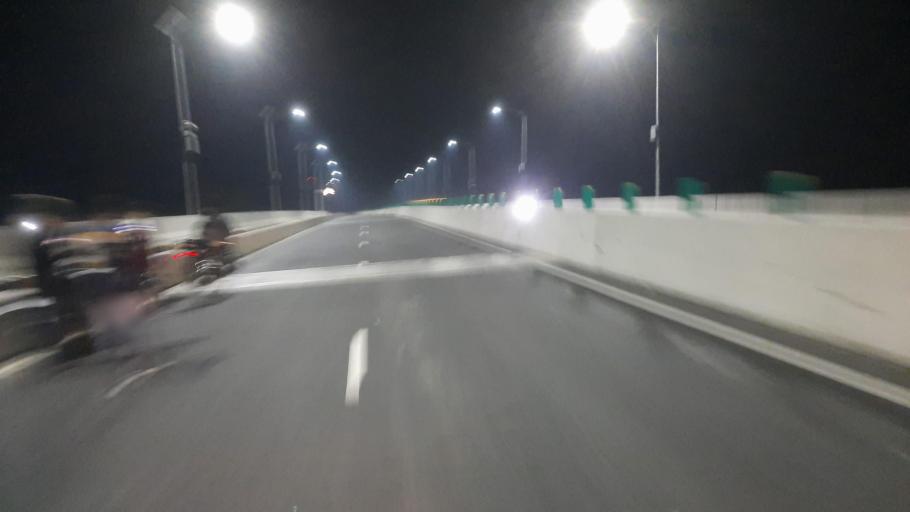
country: BD
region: Khulna
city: Kalia
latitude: 23.1931
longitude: 89.6896
